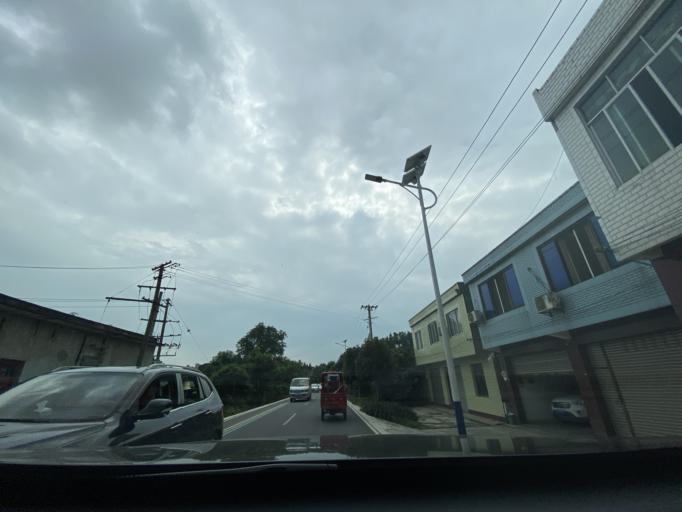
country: CN
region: Sichuan
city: Wujin
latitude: 30.4021
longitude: 103.9872
